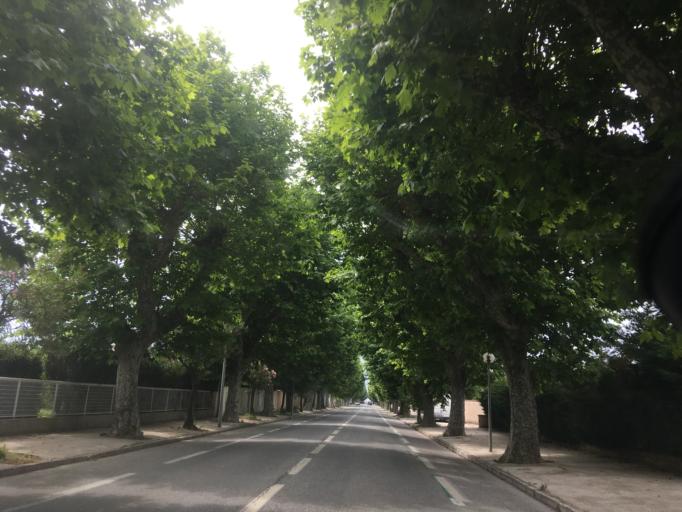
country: FR
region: Provence-Alpes-Cote d'Azur
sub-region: Departement du Var
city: La Londe-les-Maures
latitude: 43.1220
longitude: 6.2456
